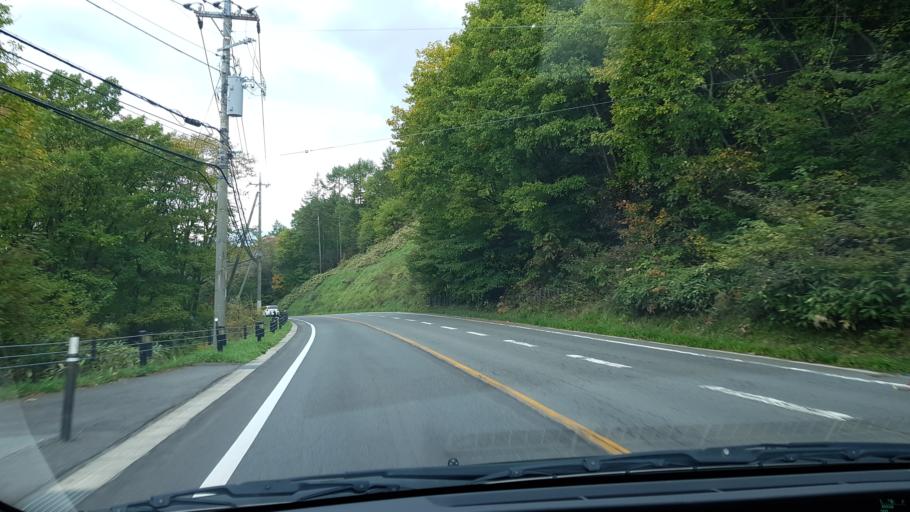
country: JP
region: Gunma
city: Nakanojomachi
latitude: 36.6057
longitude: 138.5838
